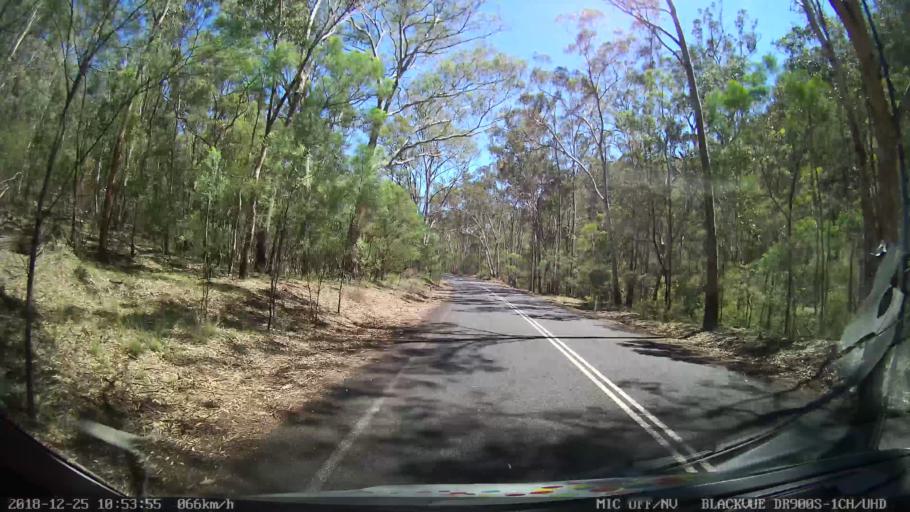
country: AU
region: New South Wales
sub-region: Upper Hunter Shire
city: Merriwa
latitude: -32.4154
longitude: 150.2729
